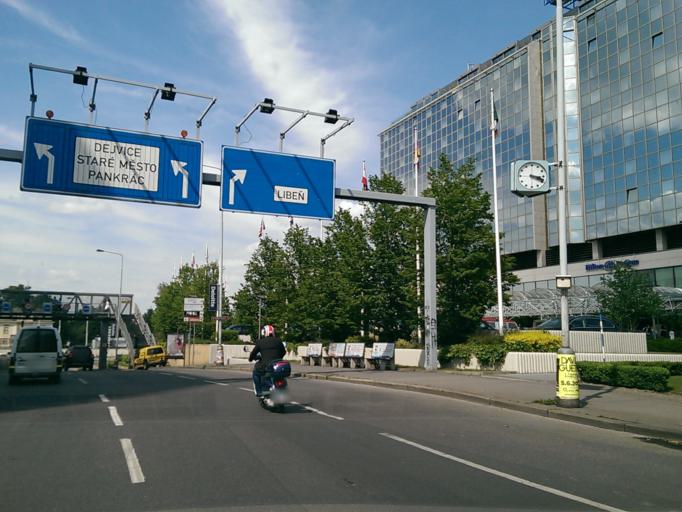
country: CZ
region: Praha
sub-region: Praha 8
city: Karlin
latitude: 50.0927
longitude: 14.4385
